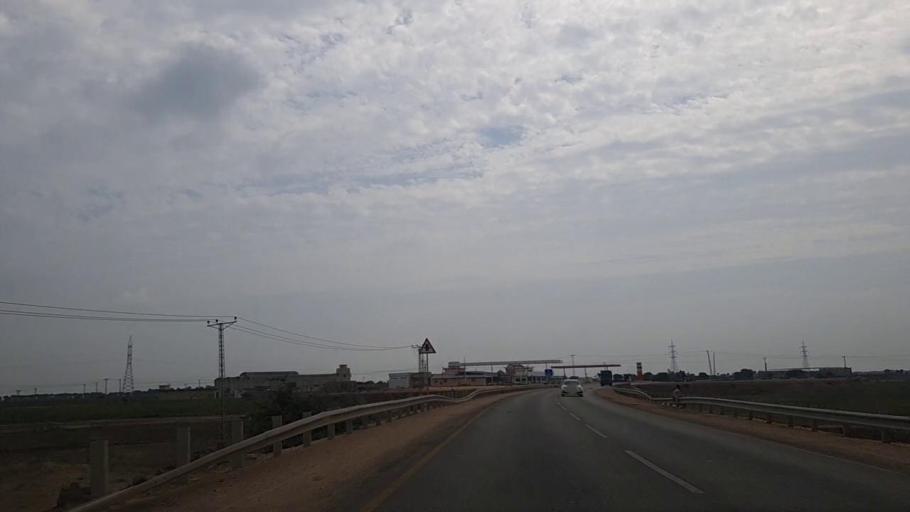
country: PK
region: Sindh
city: Daro Mehar
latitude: 24.6164
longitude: 68.0877
